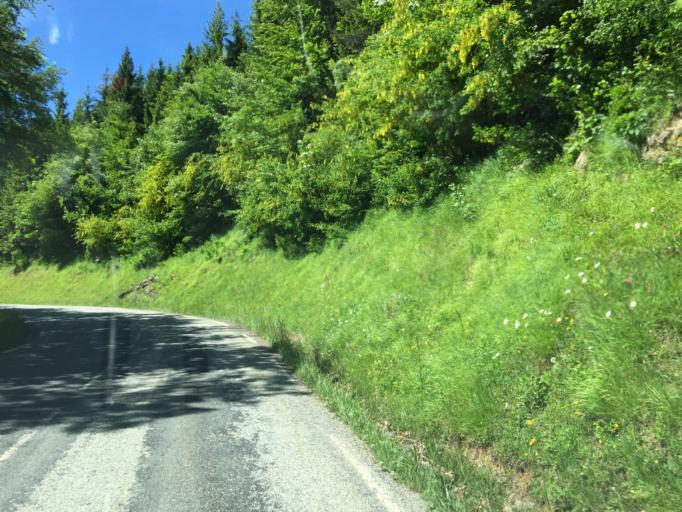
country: FR
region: Rhone-Alpes
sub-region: Departement de la Savoie
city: Saint-Baldoph
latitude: 45.4840
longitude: 5.9164
